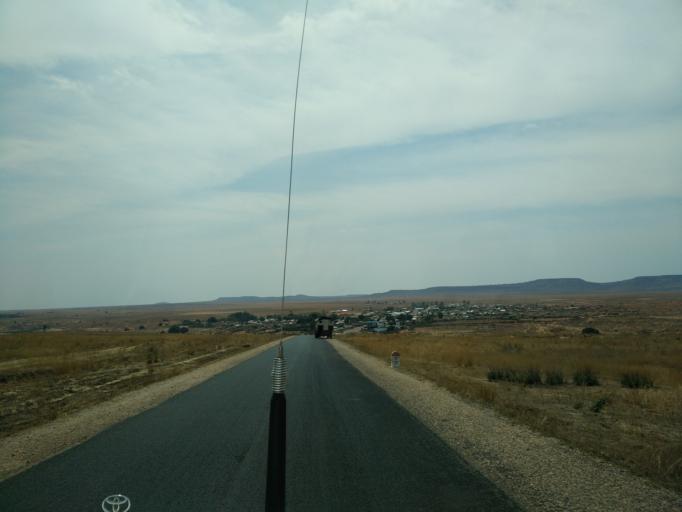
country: MG
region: Ihorombe
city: Ranohira
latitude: -22.7729
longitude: 45.0983
